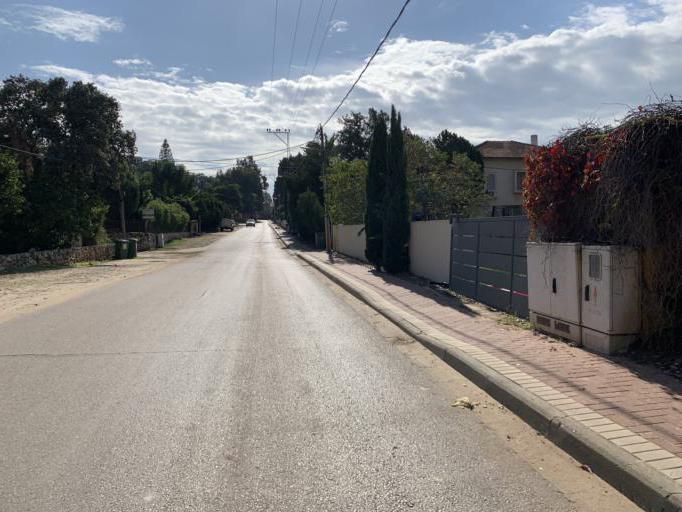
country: IL
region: Central District
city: Ra'anana
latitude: 32.1697
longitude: 34.8754
